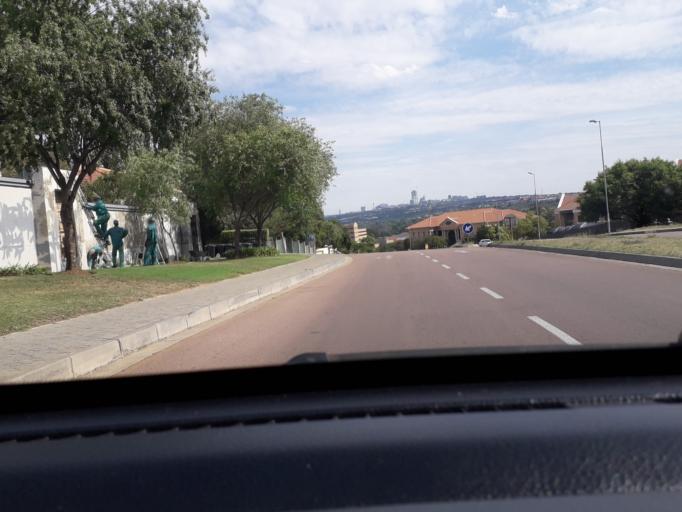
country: ZA
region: Gauteng
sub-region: City of Johannesburg Metropolitan Municipality
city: Midrand
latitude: -26.0327
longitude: 28.0696
